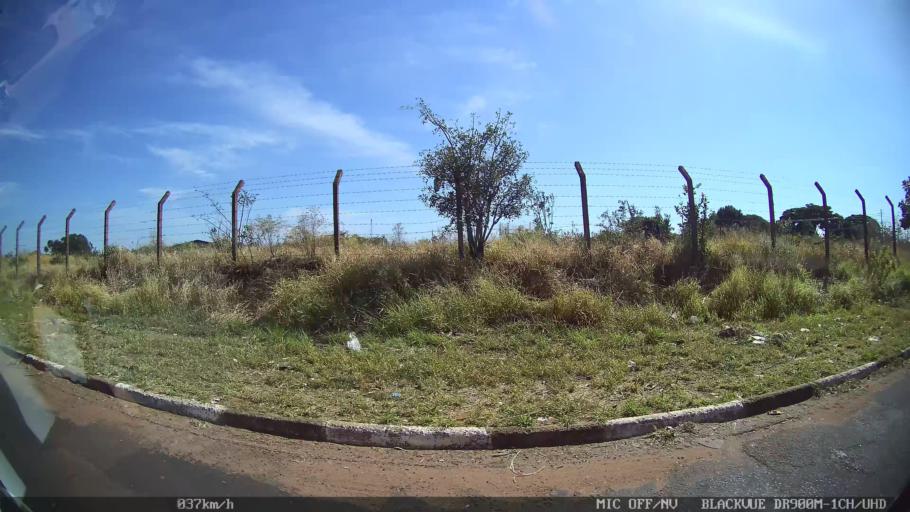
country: BR
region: Sao Paulo
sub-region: Franca
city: Franca
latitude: -20.5444
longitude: -47.4588
